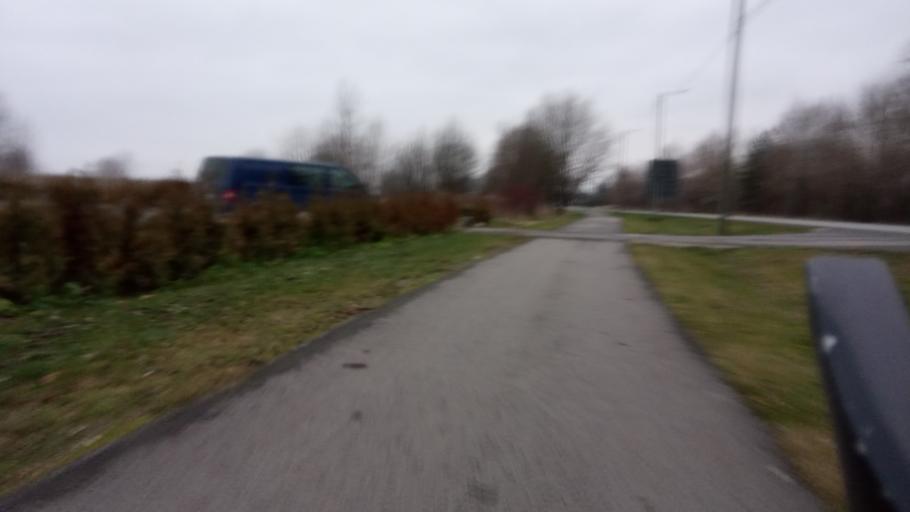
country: EE
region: Harju
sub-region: Kuusalu vald
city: Kuusalu
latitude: 59.4512
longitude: 25.4331
